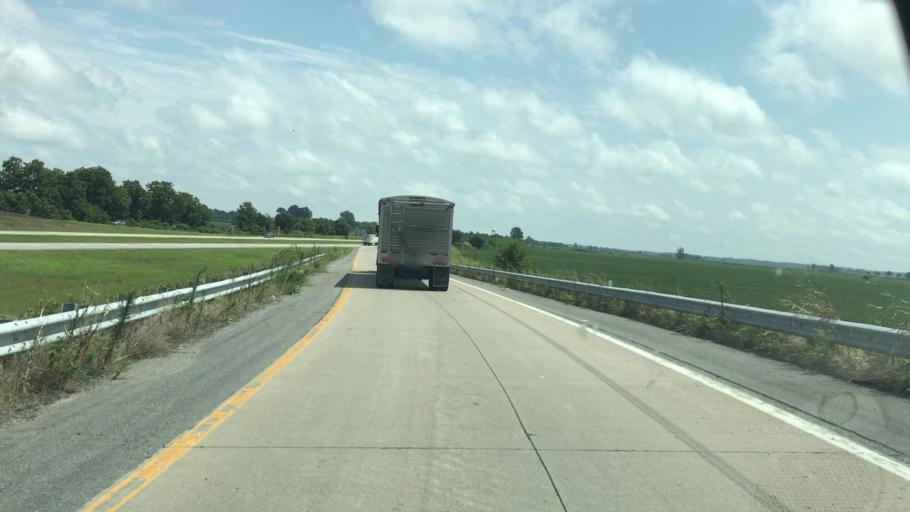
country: US
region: Missouri
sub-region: Pemiscot County
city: Caruthersville
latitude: 36.1754
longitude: -89.6937
